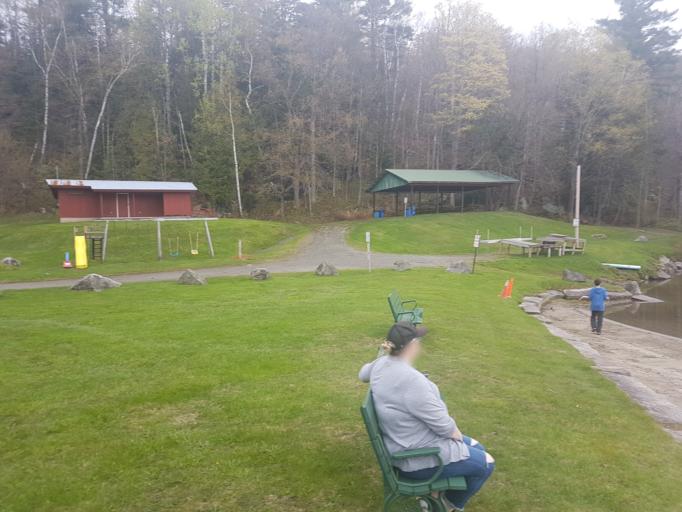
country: US
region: Vermont
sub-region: Orleans County
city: Newport
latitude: 44.7485
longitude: -72.1623
